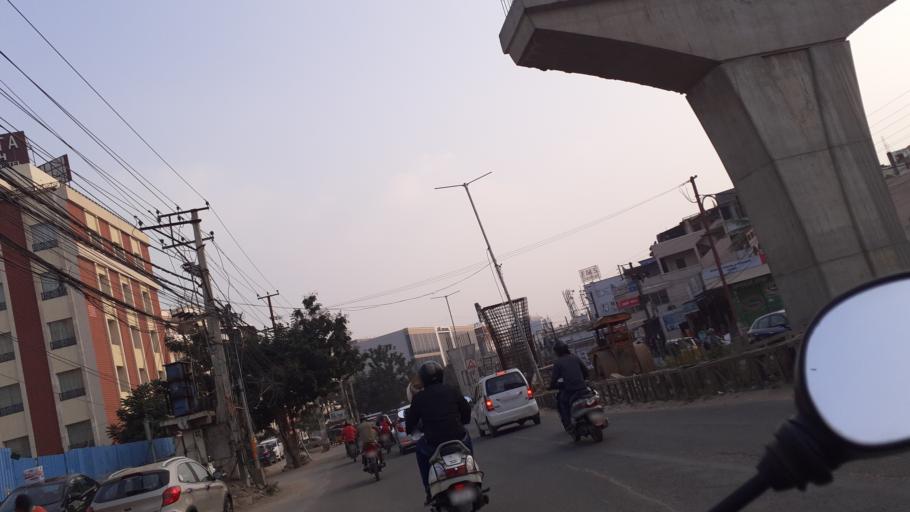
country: IN
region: Telangana
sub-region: Rangareddi
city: Kukatpalli
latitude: 17.4672
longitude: 78.3671
